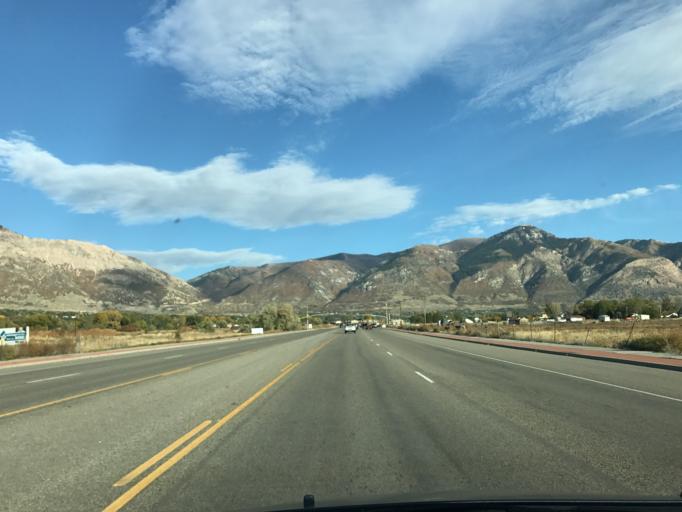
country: US
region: Utah
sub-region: Weber County
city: Pleasant View
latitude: 41.3066
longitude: -111.9952
